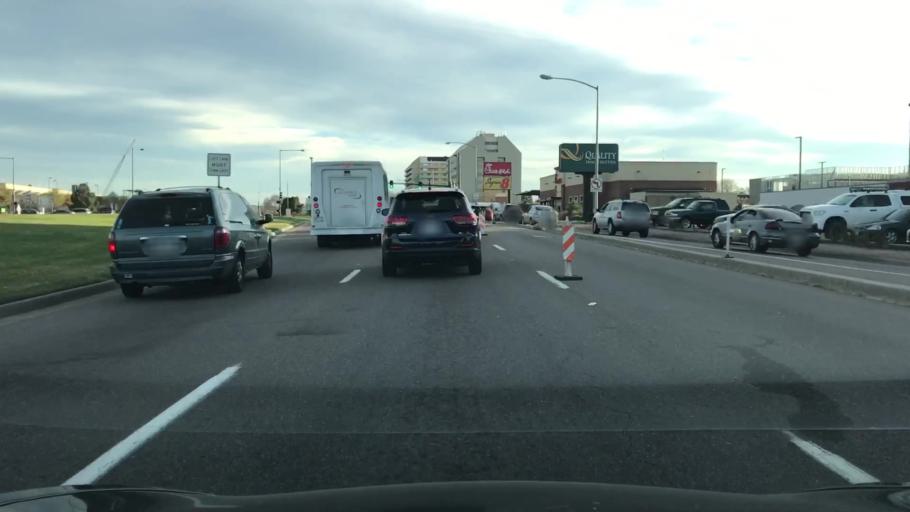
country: US
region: Colorado
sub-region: Adams County
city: Commerce City
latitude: 39.7688
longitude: -104.9034
